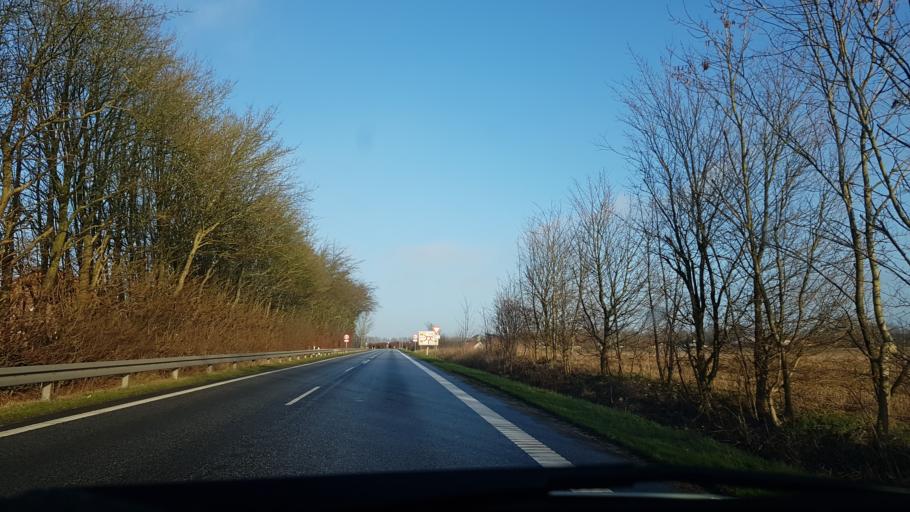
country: DK
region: South Denmark
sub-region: Tonder Kommune
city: Toftlund
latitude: 55.2513
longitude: 9.1427
